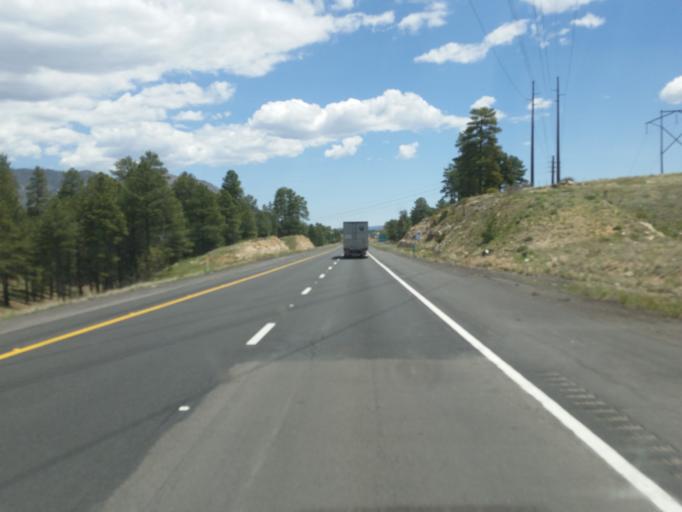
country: US
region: Arizona
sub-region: Coconino County
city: Flagstaff
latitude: 35.1794
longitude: -111.6386
